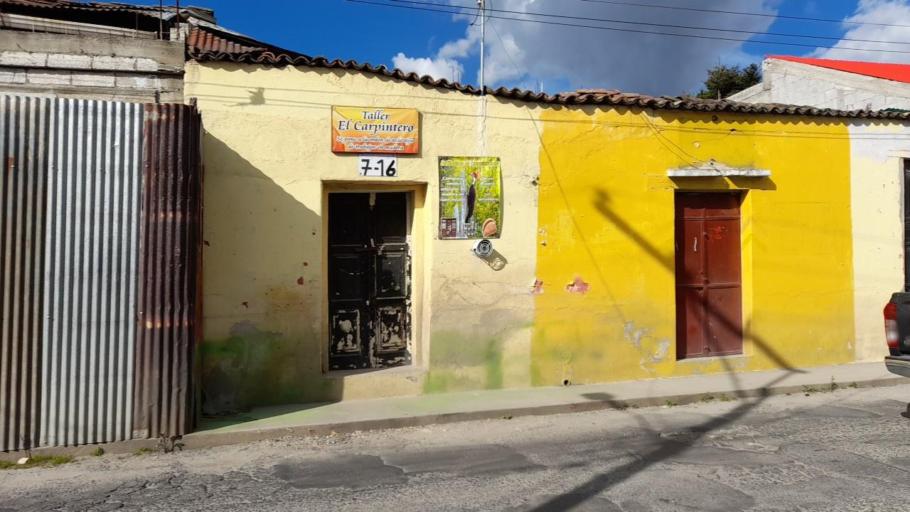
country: GT
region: Quetzaltenango
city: Quetzaltenango
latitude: 14.8314
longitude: -91.5164
